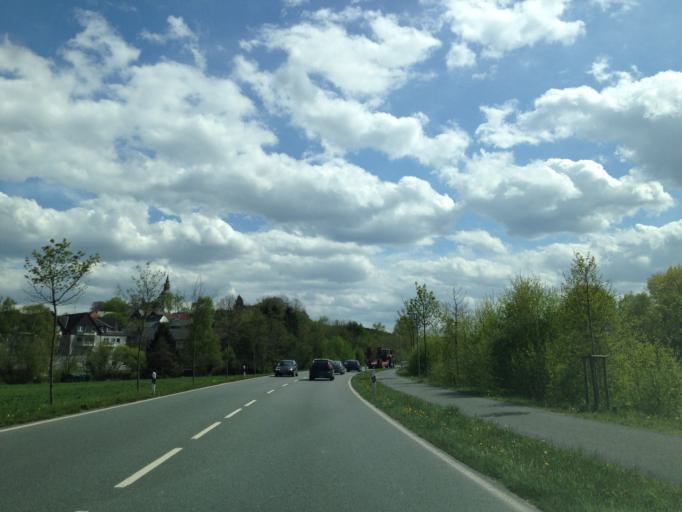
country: DE
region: North Rhine-Westphalia
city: Warstein
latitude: 51.4870
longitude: 8.3332
